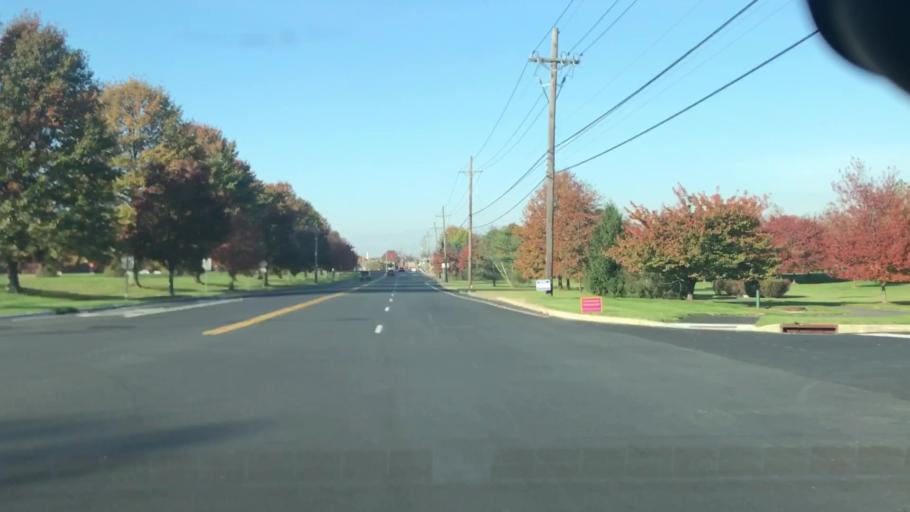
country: US
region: New Jersey
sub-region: Middlesex County
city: Plainsboro Center
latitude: 40.3356
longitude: -74.5819
